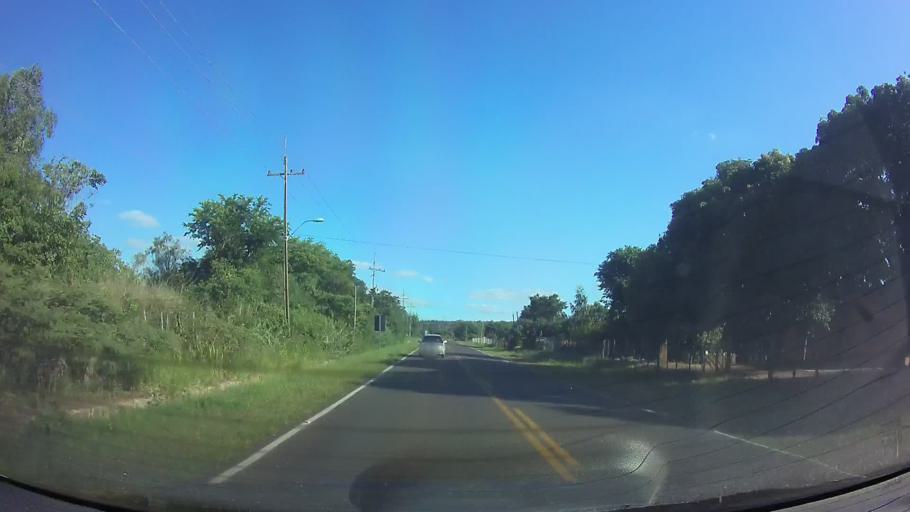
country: PY
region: Cordillera
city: Atyra
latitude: -25.2970
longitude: -57.1627
